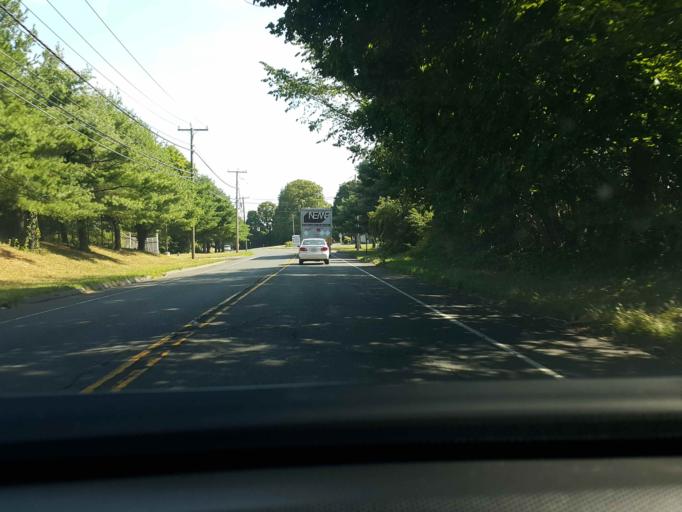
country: US
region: Connecticut
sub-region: Middlesex County
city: Durham
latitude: 41.5019
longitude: -72.6738
